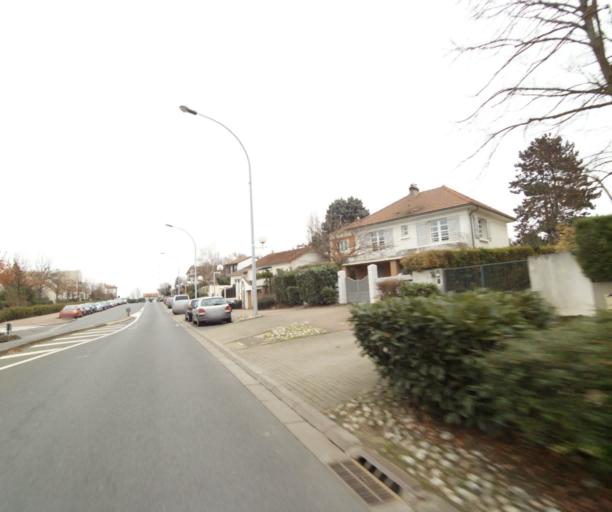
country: FR
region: Ile-de-France
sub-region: Departement des Hauts-de-Seine
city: Saint-Cloud
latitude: 48.8477
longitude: 2.1987
